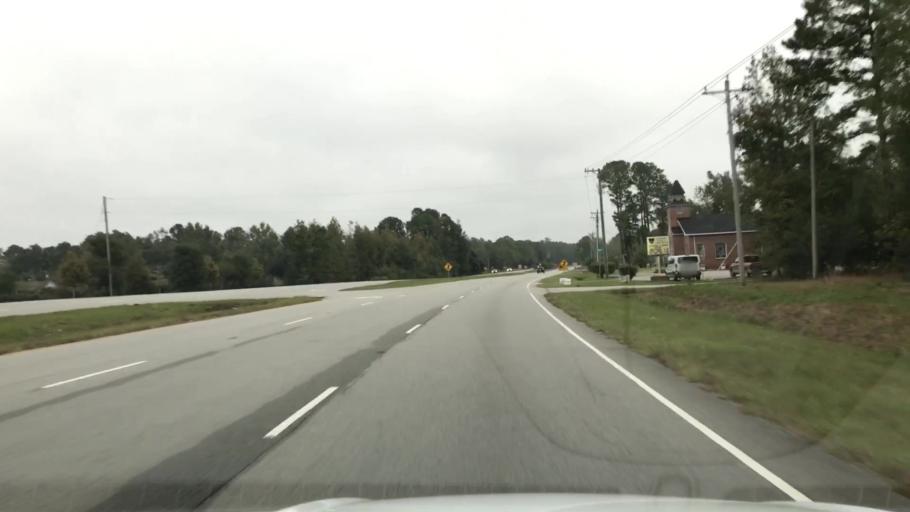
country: US
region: South Carolina
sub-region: Charleston County
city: Awendaw
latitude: 33.0271
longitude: -79.6281
